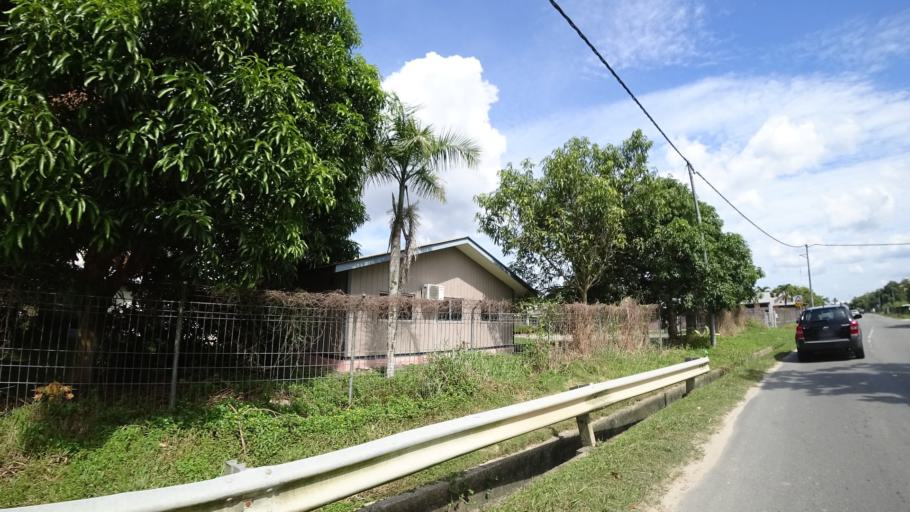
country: BN
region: Brunei and Muara
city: Bandar Seri Begawan
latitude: 4.8973
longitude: 114.8497
